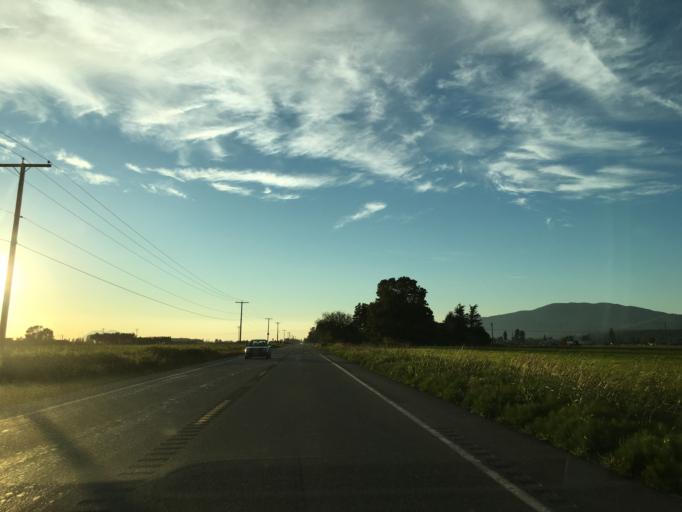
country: US
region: Washington
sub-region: Skagit County
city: Burlington
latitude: 48.5281
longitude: -122.3890
